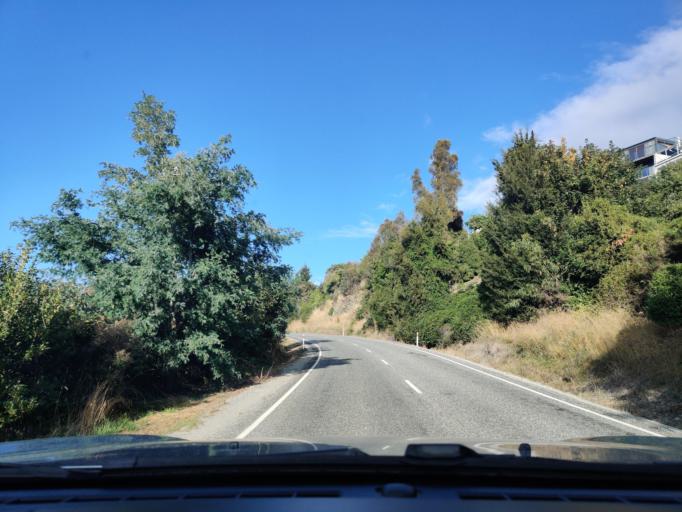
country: NZ
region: Otago
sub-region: Queenstown-Lakes District
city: Queenstown
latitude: -45.0408
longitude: 168.6375
